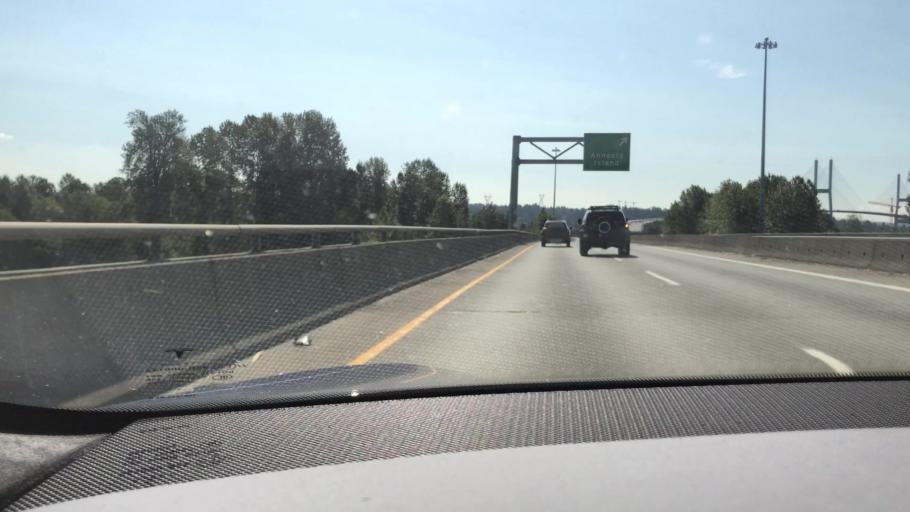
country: CA
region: British Columbia
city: New Westminster
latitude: 49.1747
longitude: -122.9585
